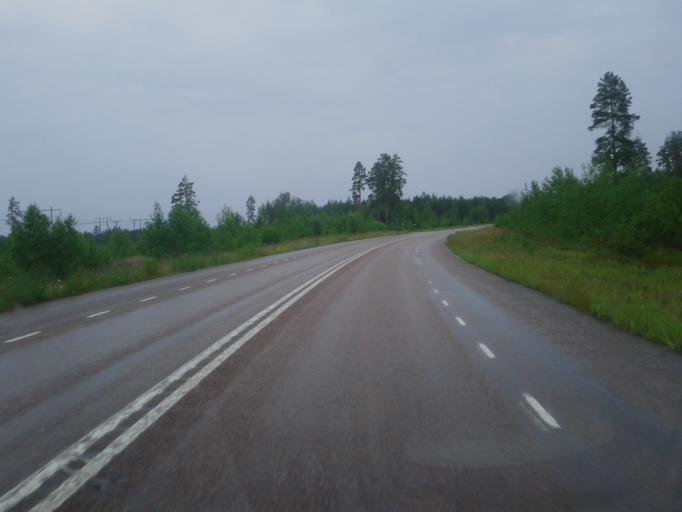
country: SE
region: Uppsala
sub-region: Alvkarleby Kommun
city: AElvkarleby
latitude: 60.5204
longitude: 17.4282
